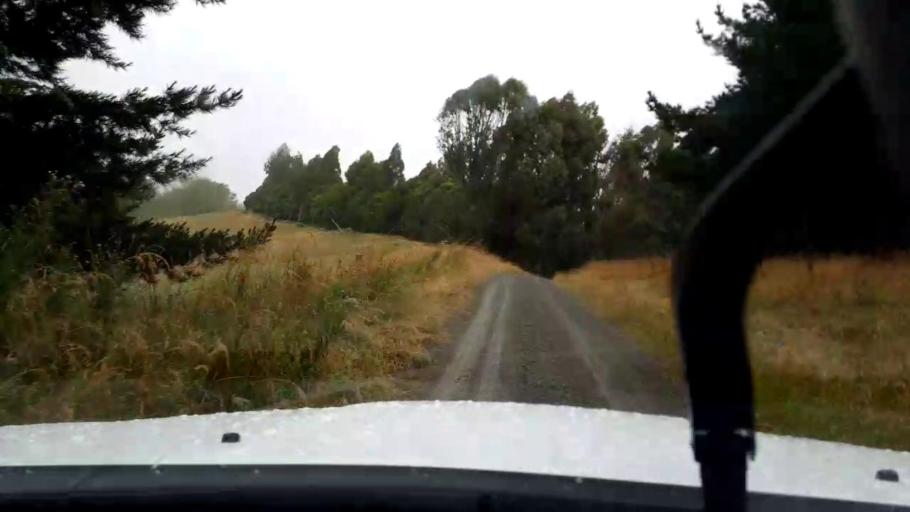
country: NZ
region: Canterbury
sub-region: Timaru District
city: Pleasant Point
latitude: -44.1848
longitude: 171.1031
